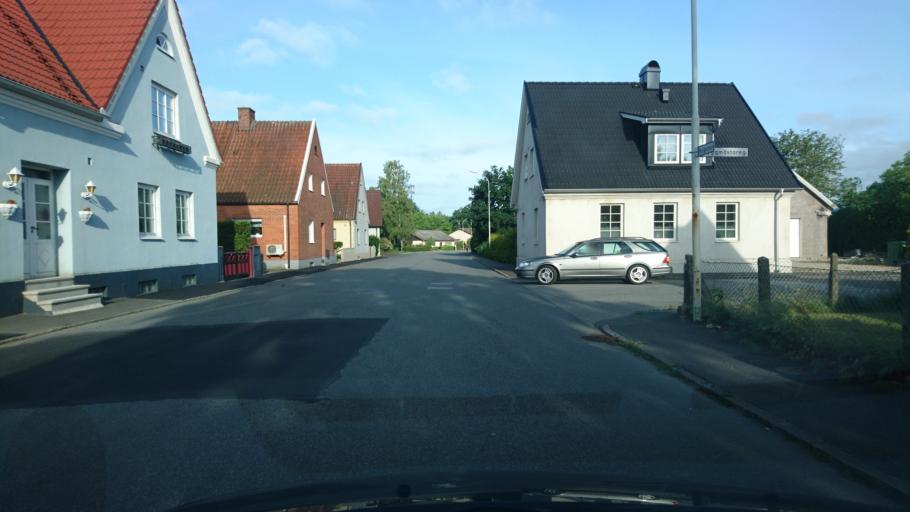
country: SE
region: Skane
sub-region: Tomelilla Kommun
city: Tomelilla
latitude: 55.5411
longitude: 13.9633
